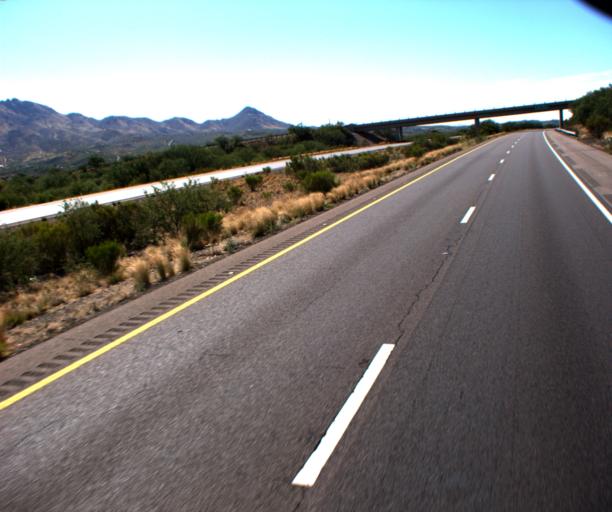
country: US
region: Arizona
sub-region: Santa Cruz County
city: Rio Rico
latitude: 31.5290
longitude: -111.0259
